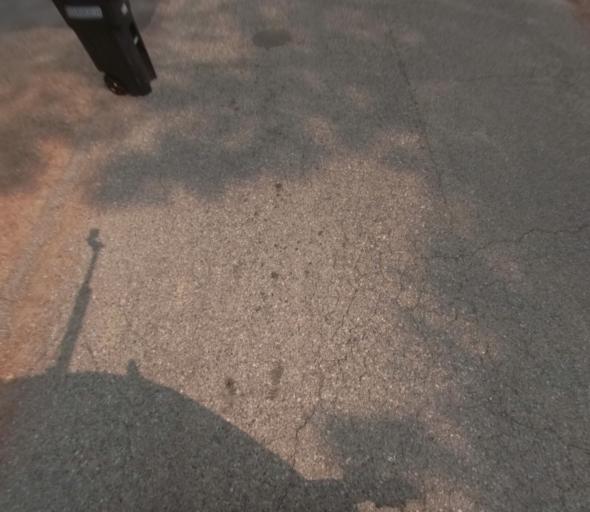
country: US
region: California
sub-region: Madera County
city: Coarsegold
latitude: 37.2096
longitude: -119.6857
